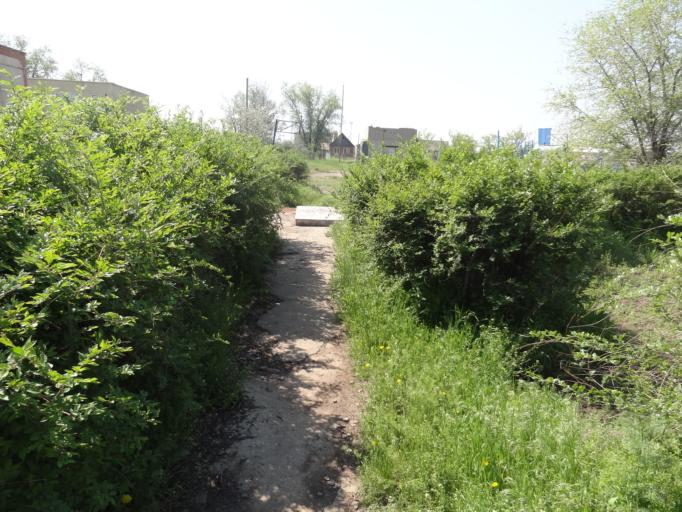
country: RU
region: Saratov
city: Privolzhskiy
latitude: 51.4108
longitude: 46.0955
